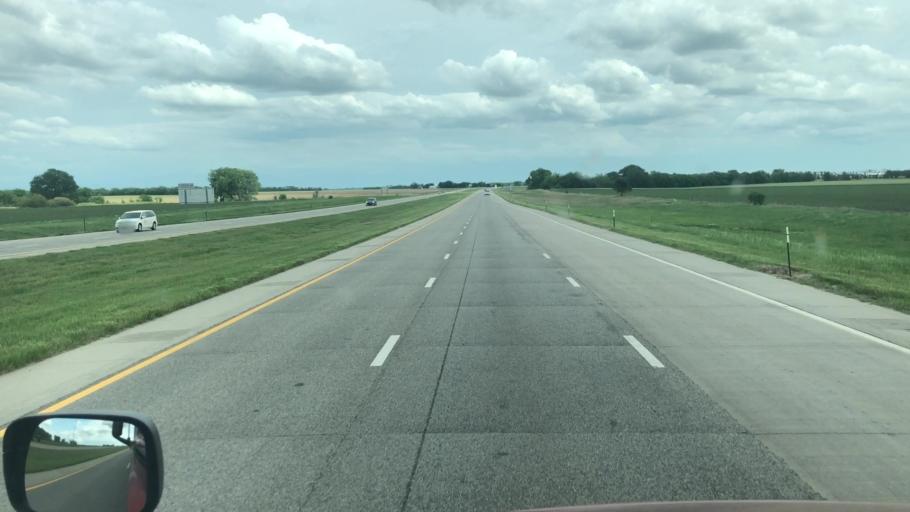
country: US
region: Kansas
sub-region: McPherson County
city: Moundridge
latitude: 38.2283
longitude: -97.5160
